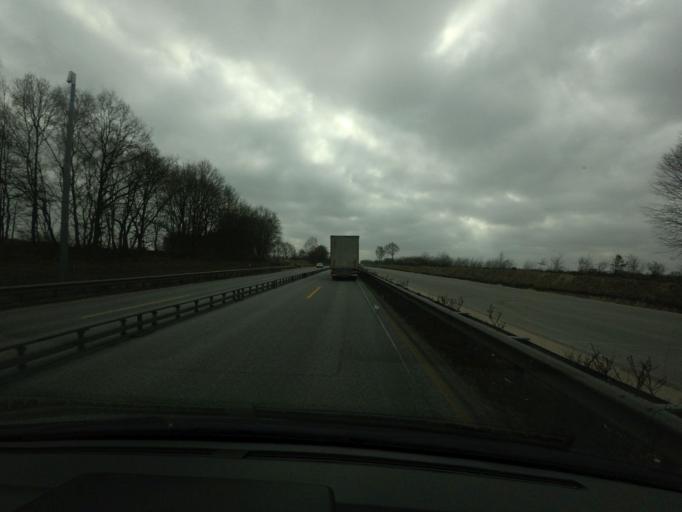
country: DE
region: Schleswig-Holstein
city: Alveslohe
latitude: 53.7800
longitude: 9.9416
